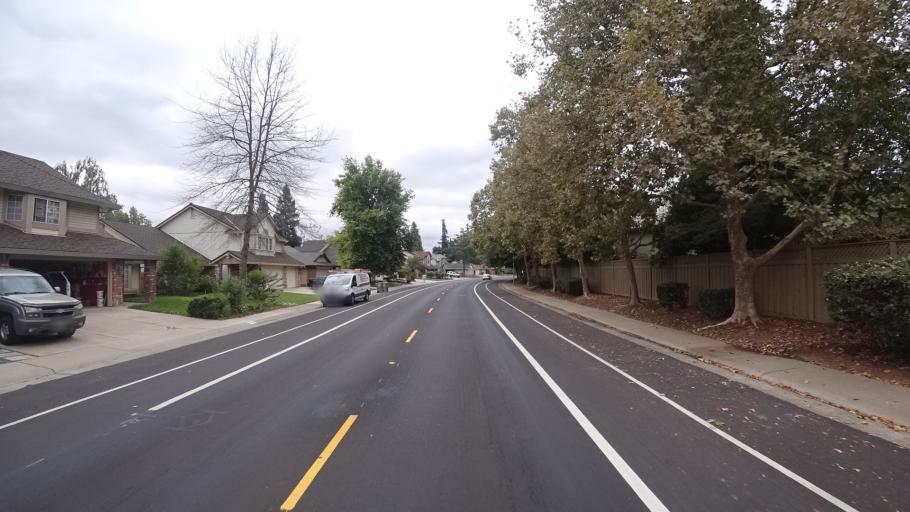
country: US
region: California
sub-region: Sacramento County
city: Laguna
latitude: 38.4163
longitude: -121.4301
